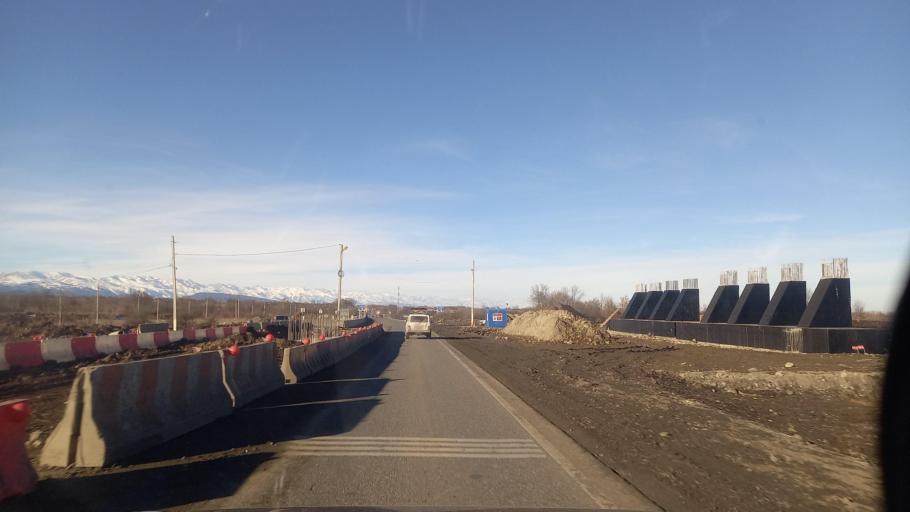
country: RU
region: North Ossetia
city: Gizel'
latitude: 43.0276
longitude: 44.6071
